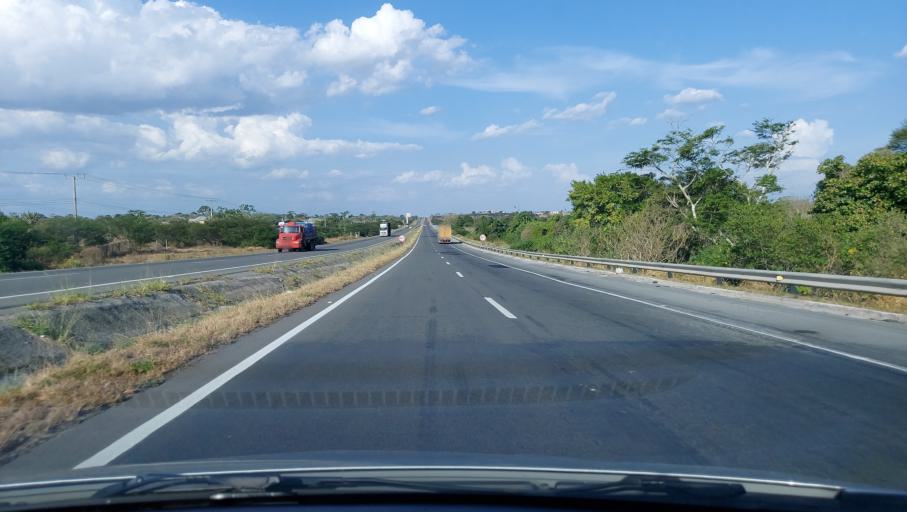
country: BR
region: Bahia
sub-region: Santo Estevao
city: Santo Estevao
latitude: -12.3776
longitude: -39.1235
